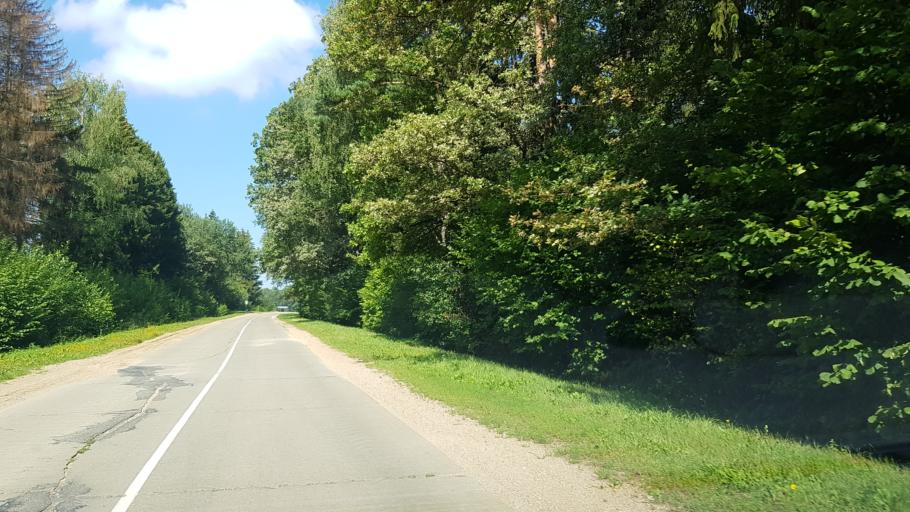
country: BY
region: Minsk
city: Dzyarzhynsk
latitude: 53.7086
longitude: 27.0789
